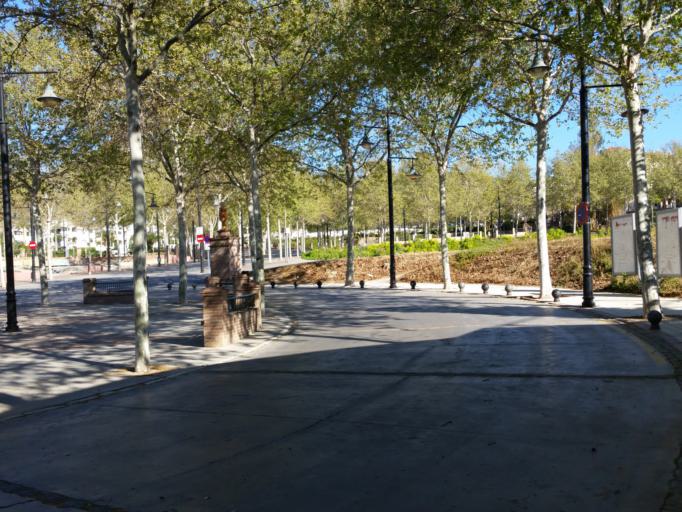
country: ES
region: Andalusia
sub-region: Provincia de Malaga
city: Benalmadena
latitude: 36.5930
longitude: -4.5317
